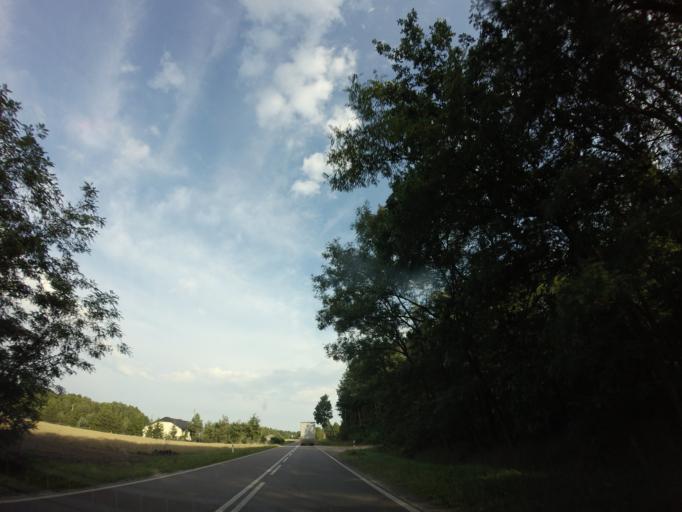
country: PL
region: Lublin Voivodeship
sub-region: Powiat lubartowski
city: Jeziorzany
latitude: 51.5770
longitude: 22.2852
